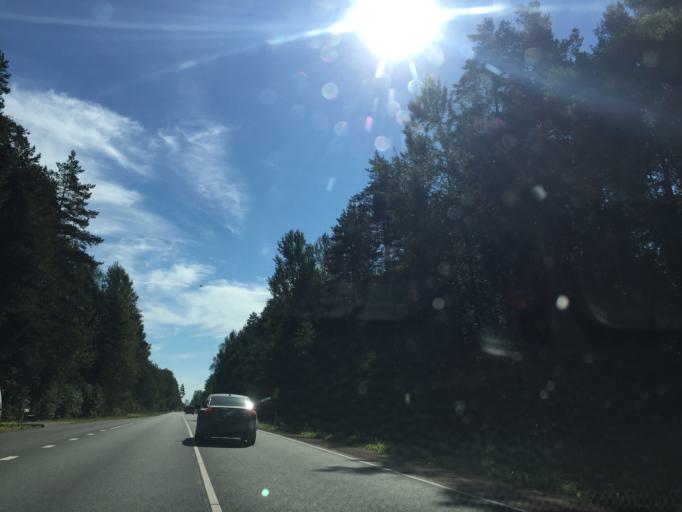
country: LV
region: Ikskile
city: Ikskile
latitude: 56.8769
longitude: 24.5243
